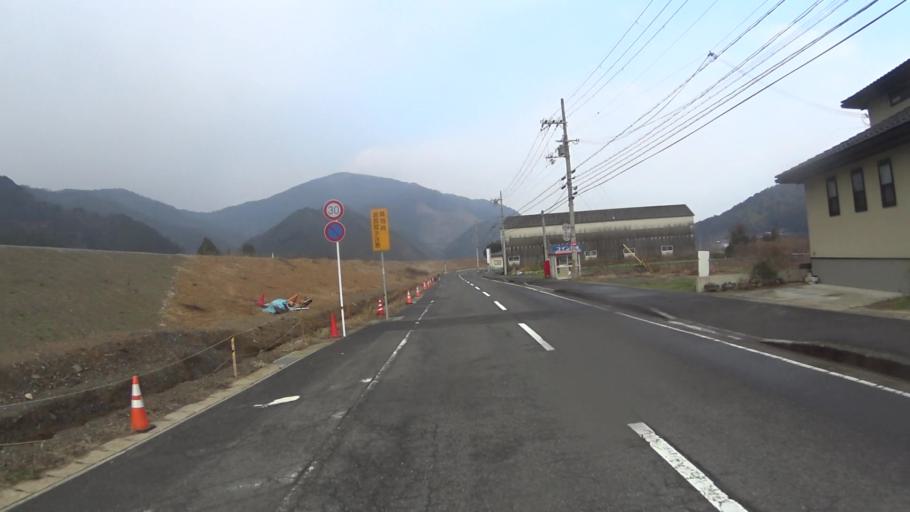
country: JP
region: Kyoto
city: Maizuru
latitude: 35.4711
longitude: 135.2820
